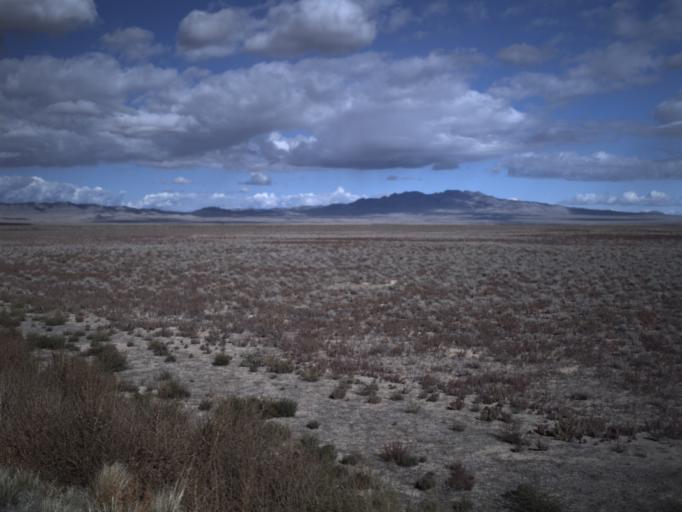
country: US
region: Utah
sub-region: Beaver County
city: Milford
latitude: 38.5218
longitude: -113.6534
